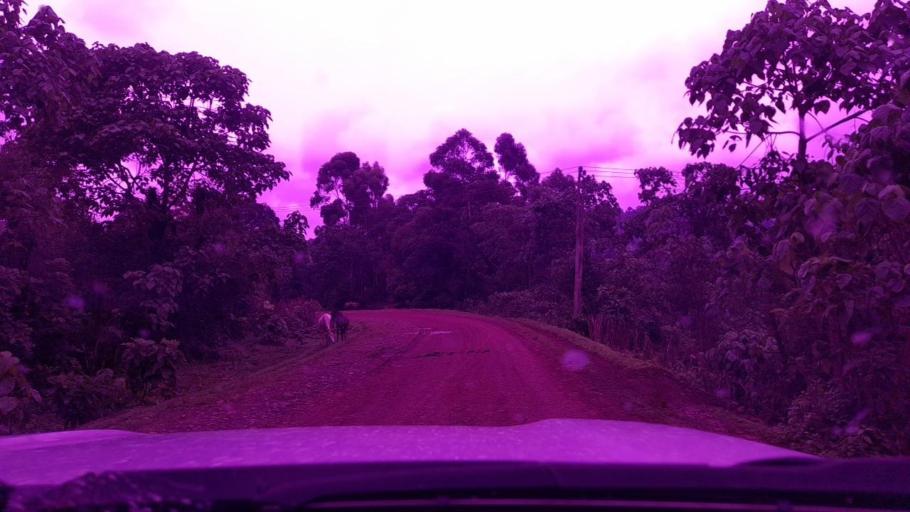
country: ET
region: Southern Nations, Nationalities, and People's Region
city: Tippi
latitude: 7.5744
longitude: 35.7806
